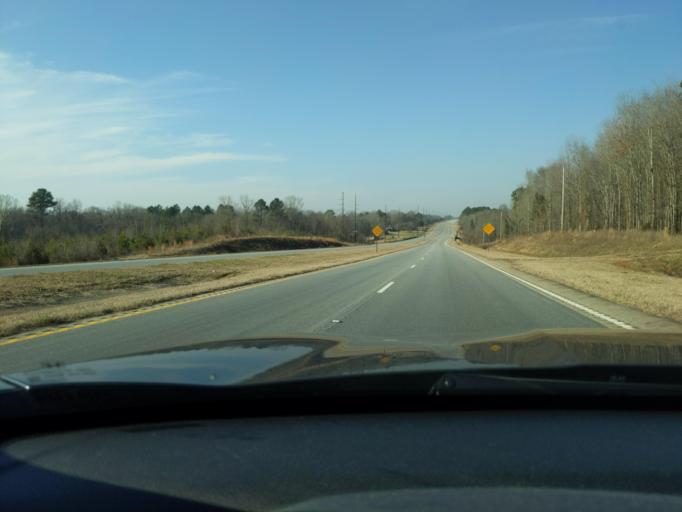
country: US
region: South Carolina
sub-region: Abbeville County
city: Calhoun Falls
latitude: 34.1068
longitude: -82.5275
